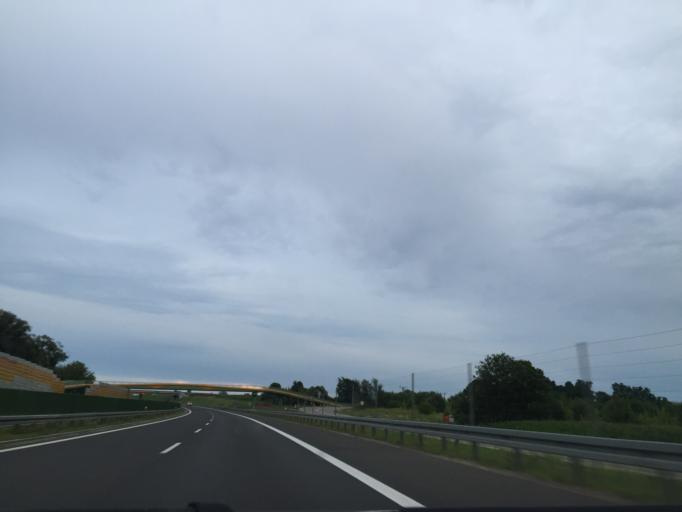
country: PL
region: Podlasie
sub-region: Powiat bialostocki
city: Choroszcz
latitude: 53.1620
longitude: 22.9745
